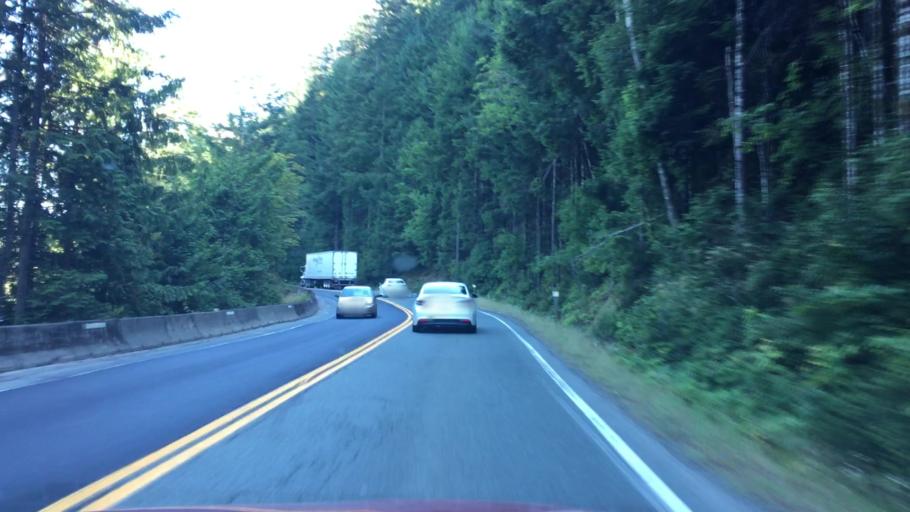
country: CA
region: British Columbia
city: Port Alberni
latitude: 49.2884
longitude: -124.6074
